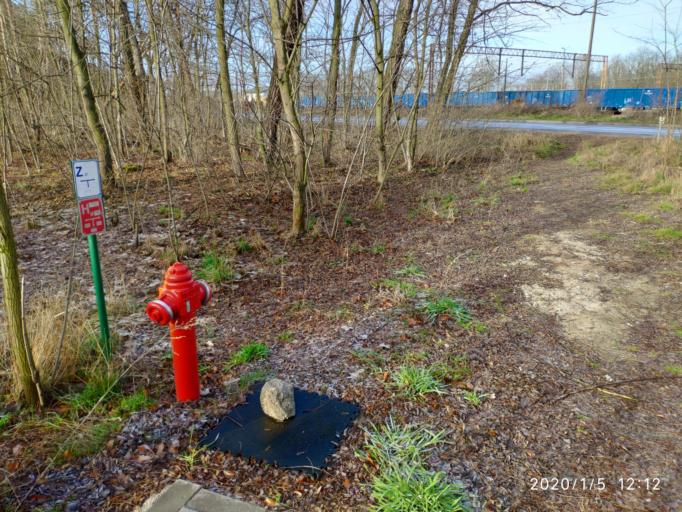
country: PL
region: Lubusz
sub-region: Powiat zielonogorski
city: Czerwiensk
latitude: 52.0147
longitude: 15.4105
